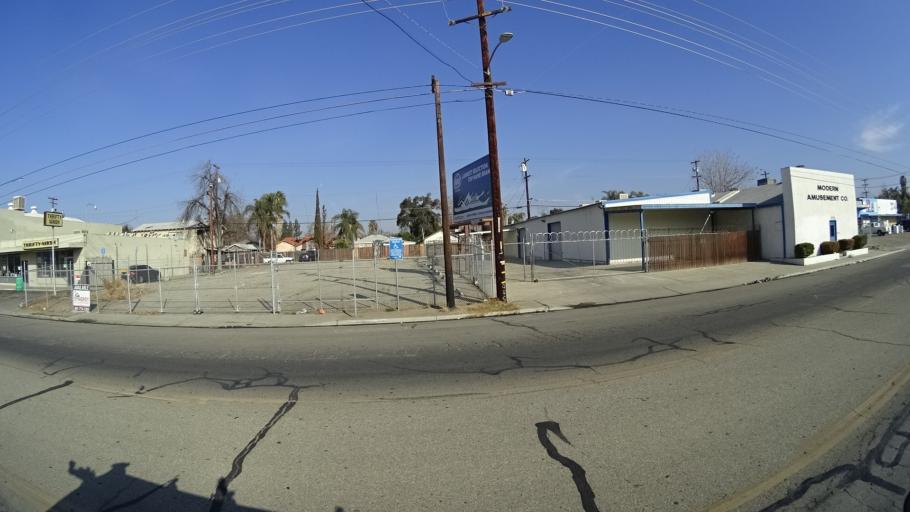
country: US
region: California
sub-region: Kern County
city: Bakersfield
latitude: 35.3903
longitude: -118.9934
